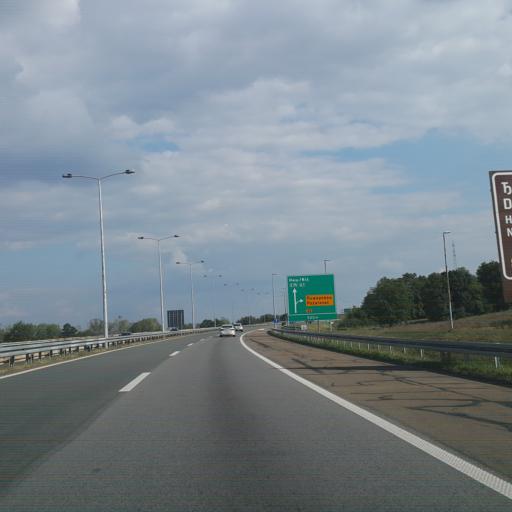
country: RS
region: Central Serbia
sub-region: Podunavski Okrug
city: Smederevo
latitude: 44.5841
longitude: 20.9672
